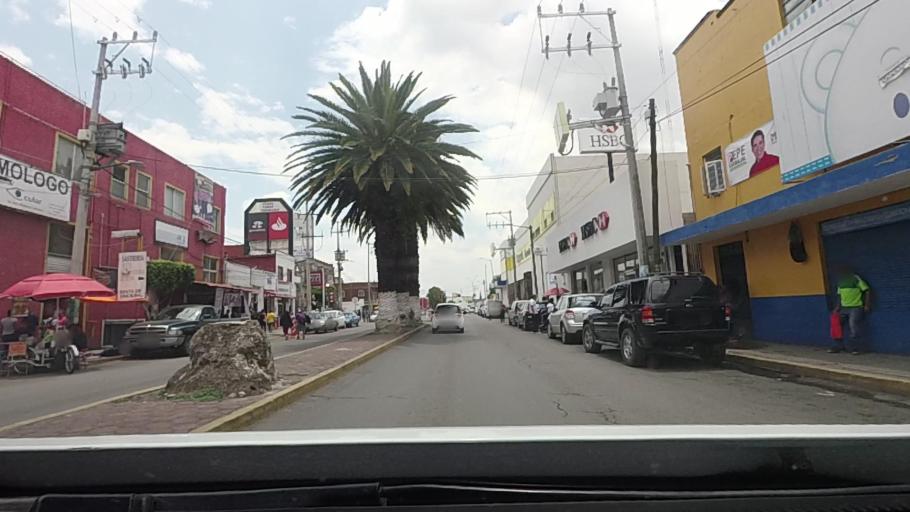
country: MX
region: Mexico
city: Chalco de Diaz Covarrubias
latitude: 19.2617
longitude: -98.8987
